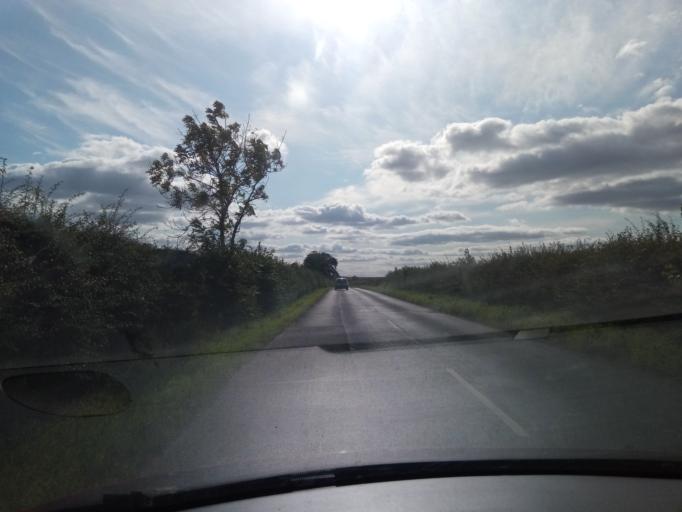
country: GB
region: Scotland
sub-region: The Scottish Borders
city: Allanton
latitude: 55.7396
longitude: -2.1908
